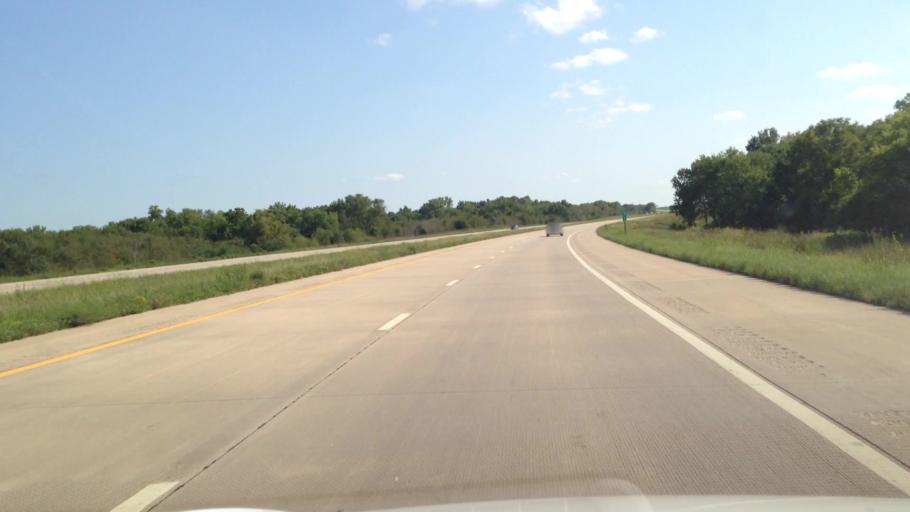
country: US
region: Kansas
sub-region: Bourbon County
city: Fort Scott
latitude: 37.9073
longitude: -94.7033
